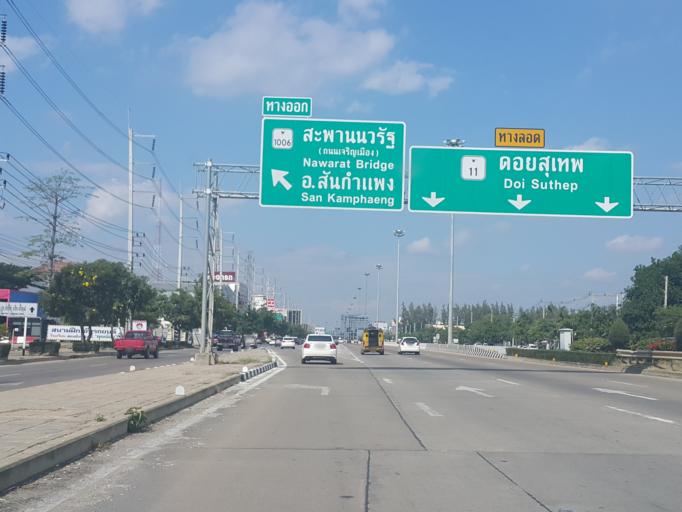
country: TH
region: Chiang Mai
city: Chiang Mai
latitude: 18.7720
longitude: 99.0282
